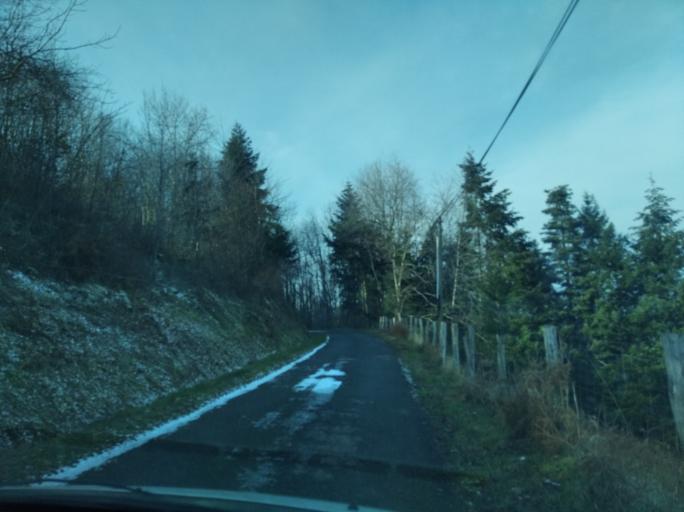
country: FR
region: Rhone-Alpes
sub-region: Departement de la Loire
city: La Pacaudiere
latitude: 46.1680
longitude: 3.7533
